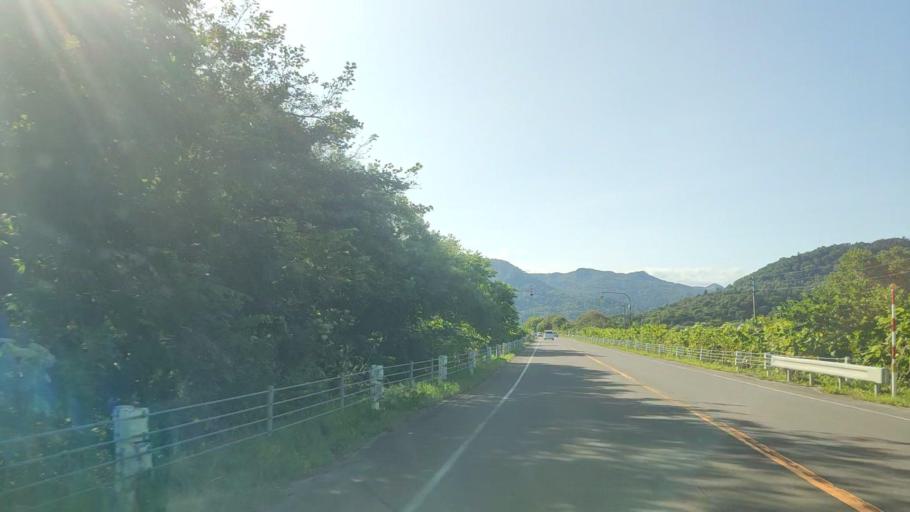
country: JP
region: Hokkaido
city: Nayoro
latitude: 44.7291
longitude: 142.2123
